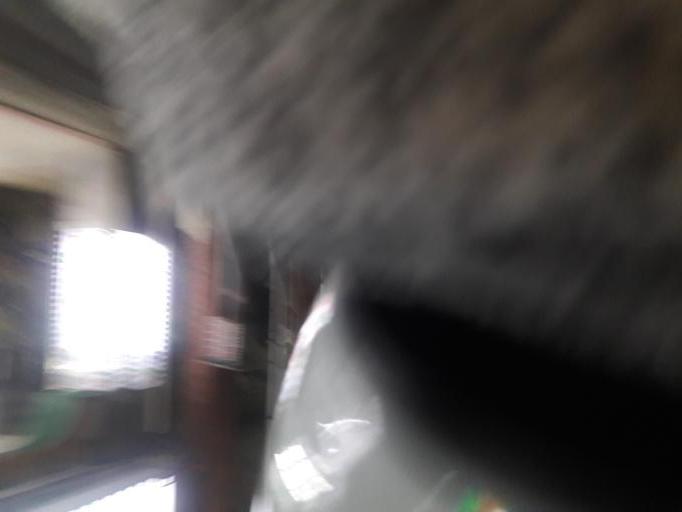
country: TW
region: Taiwan
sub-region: Miaoli
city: Miaoli
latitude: 24.4885
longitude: 120.6805
